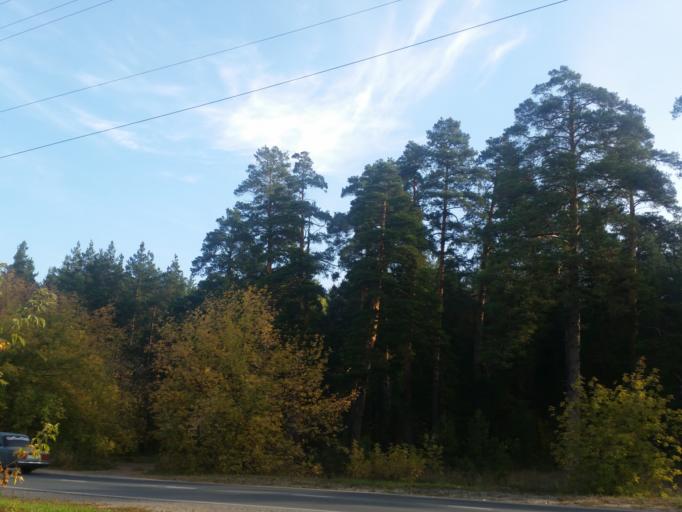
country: RU
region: Ulyanovsk
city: Dimitrovgrad
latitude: 54.2425
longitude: 49.5998
